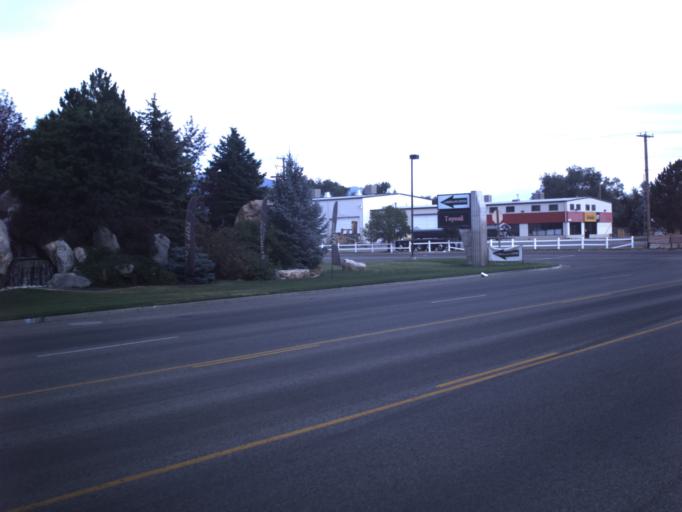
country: US
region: Utah
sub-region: Weber County
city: Marriott-Slaterville
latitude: 41.2249
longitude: -112.0257
